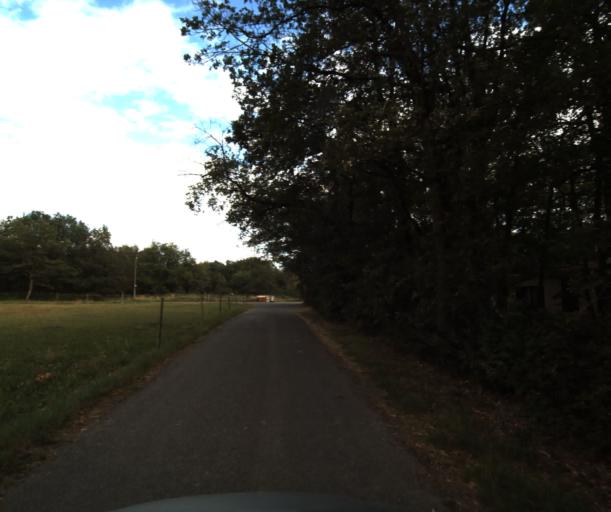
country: FR
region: Midi-Pyrenees
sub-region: Departement de la Haute-Garonne
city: Eaunes
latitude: 43.4003
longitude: 1.3394
